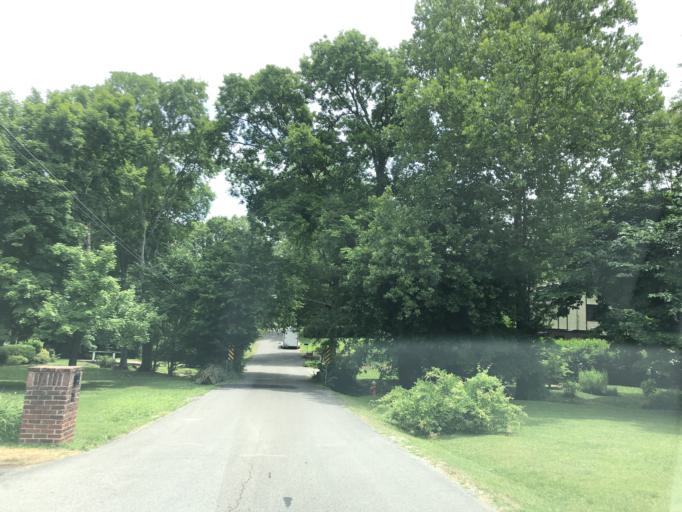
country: US
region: Tennessee
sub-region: Davidson County
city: Oak Hill
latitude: 36.1001
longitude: -86.7976
